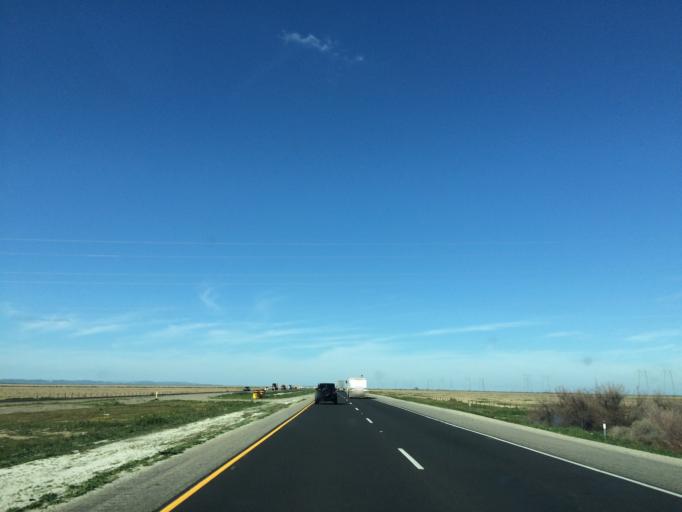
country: US
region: California
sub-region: Kings County
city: Kettleman City
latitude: 35.8306
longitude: -119.8127
